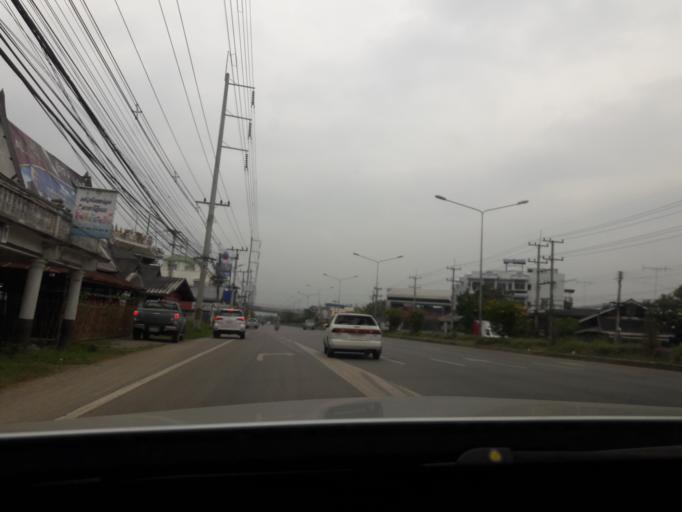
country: TH
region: Samut Songkhram
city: Samut Songkhram
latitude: 13.4175
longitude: 99.9948
